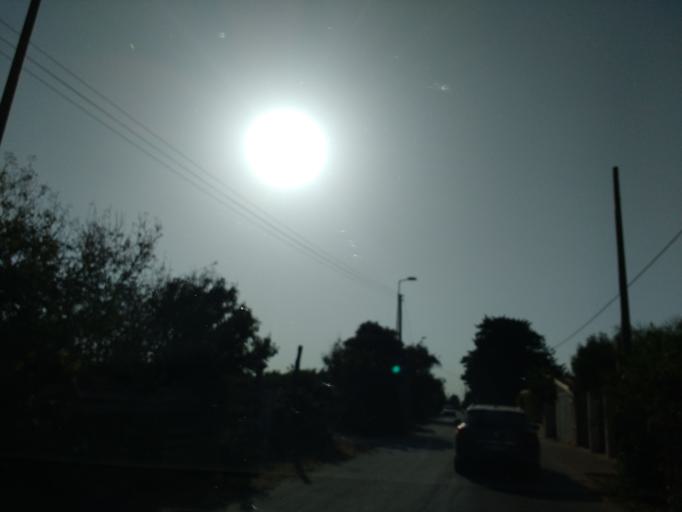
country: IT
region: Sicily
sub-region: Ragusa
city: Cava d'Aliga
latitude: 36.7439
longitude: 14.6746
